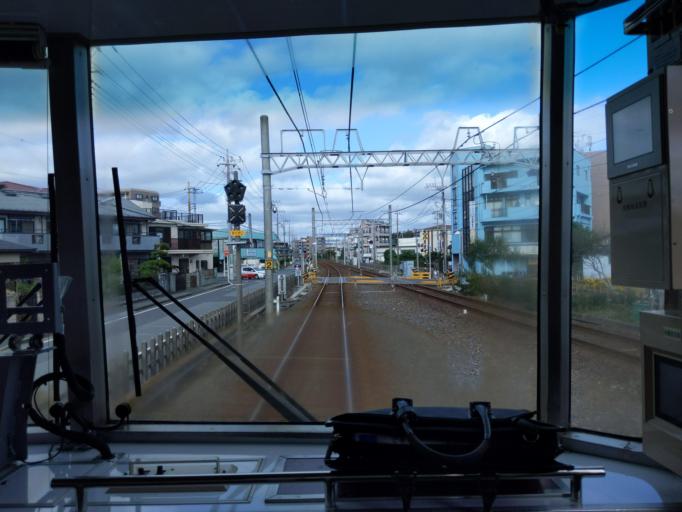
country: JP
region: Chiba
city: Funabashi
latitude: 35.7111
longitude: 140.0389
